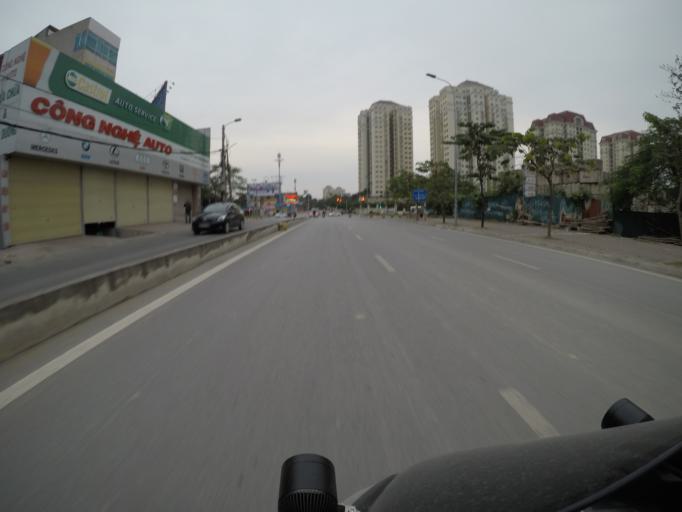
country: VN
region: Ha Noi
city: Tay Ho
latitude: 21.0702
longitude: 105.8100
